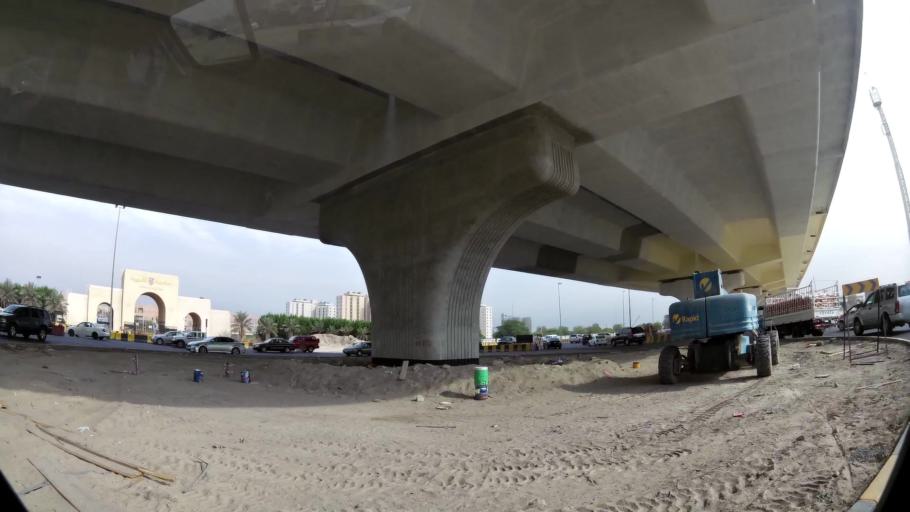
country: KW
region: Al Asimah
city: Ash Shamiyah
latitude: 29.3368
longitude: 47.9189
